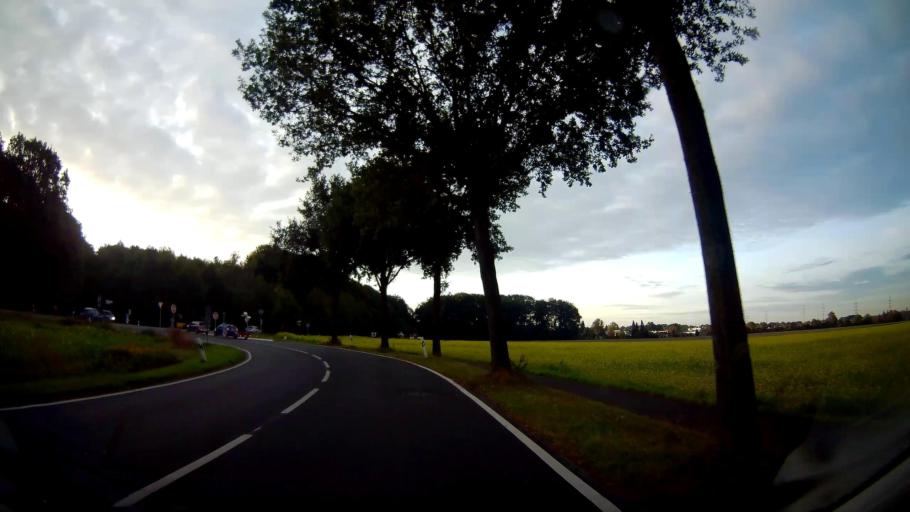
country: DE
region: North Rhine-Westphalia
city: Marl
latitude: 51.6213
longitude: 7.1096
